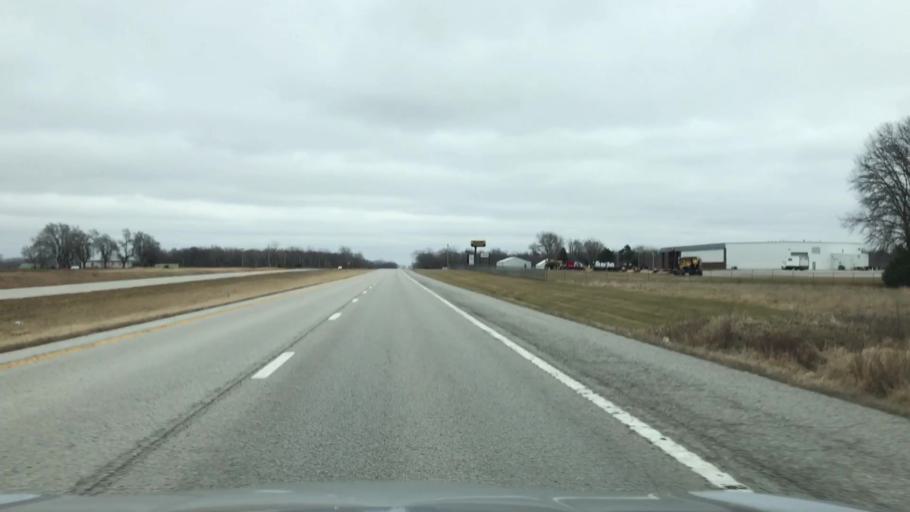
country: US
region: Missouri
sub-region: Livingston County
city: Chillicothe
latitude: 39.7766
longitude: -93.4481
